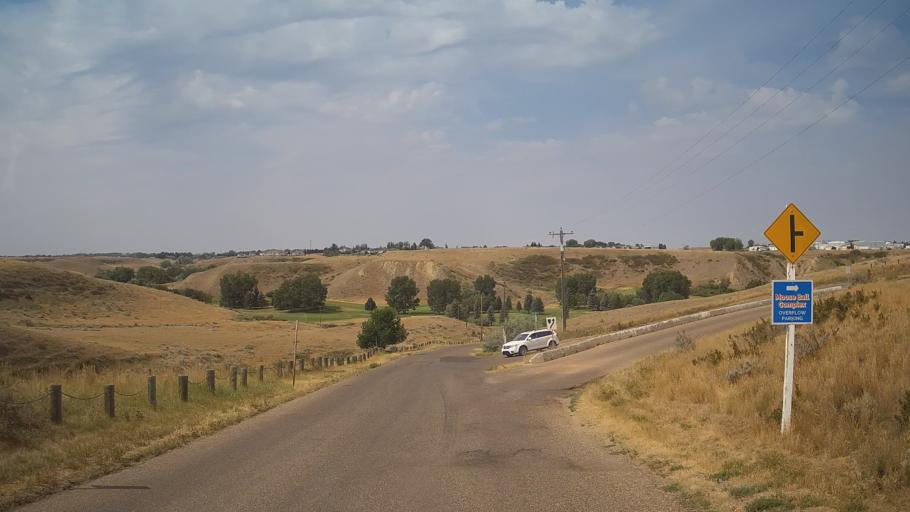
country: CA
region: Alberta
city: Medicine Hat
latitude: 50.0121
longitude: -110.6892
